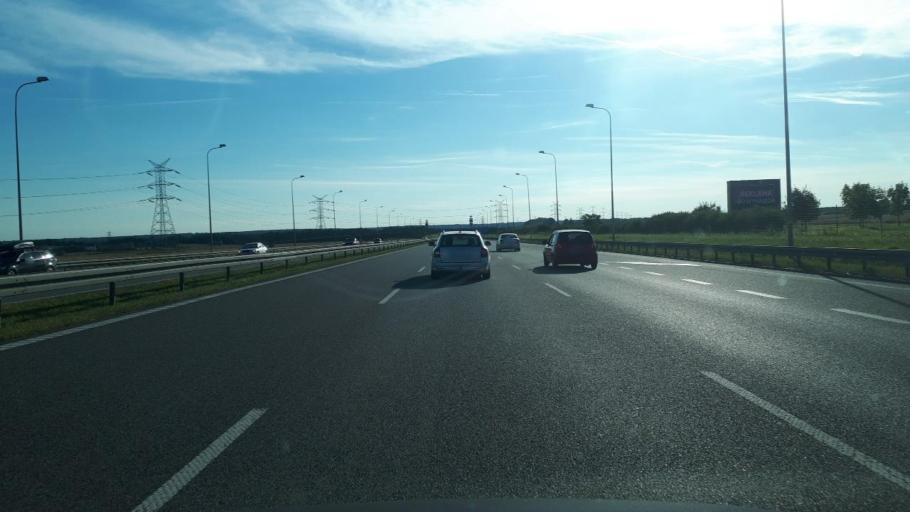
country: PL
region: Silesian Voivodeship
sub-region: Powiat tarnogorski
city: Wieszowa
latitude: 50.3746
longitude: 18.7668
